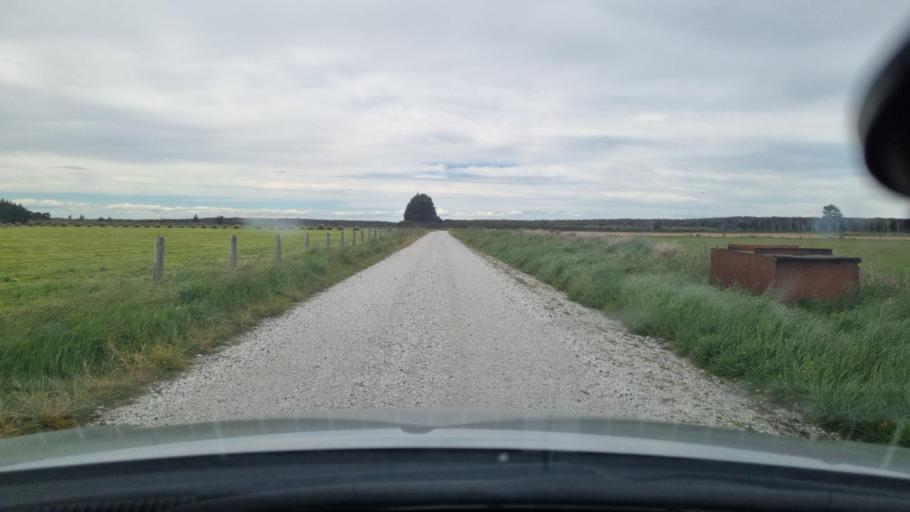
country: NZ
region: Southland
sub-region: Invercargill City
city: Invercargill
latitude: -46.5066
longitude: 168.4423
